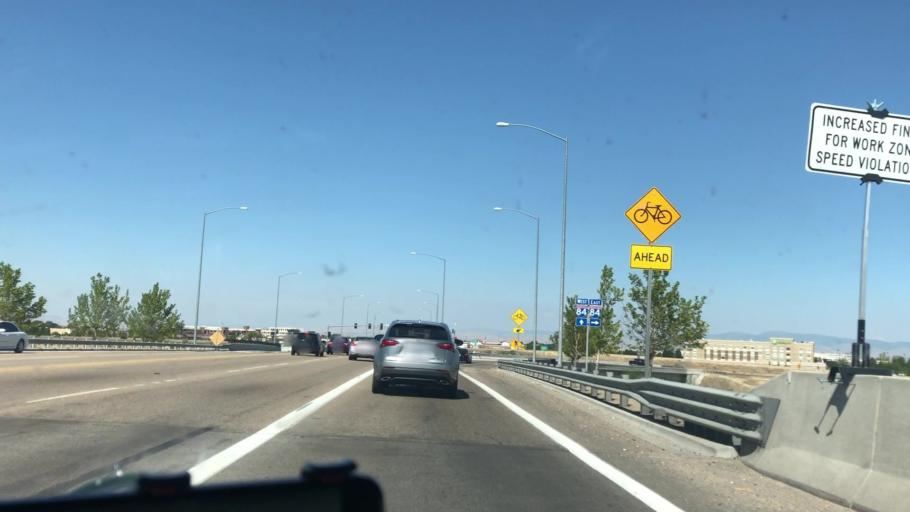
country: US
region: Idaho
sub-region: Canyon County
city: Nampa
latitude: 43.6077
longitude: -116.5994
